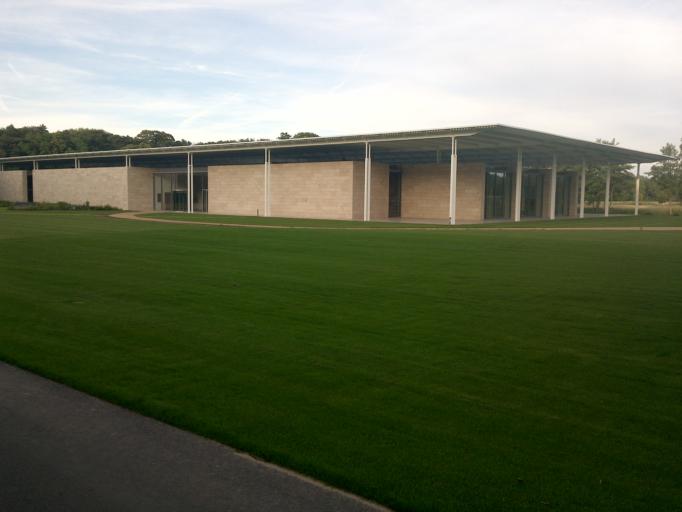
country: NL
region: South Holland
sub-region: Gemeente Leidschendam-Voorburg
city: Voorburg
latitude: 52.1191
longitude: 4.3460
